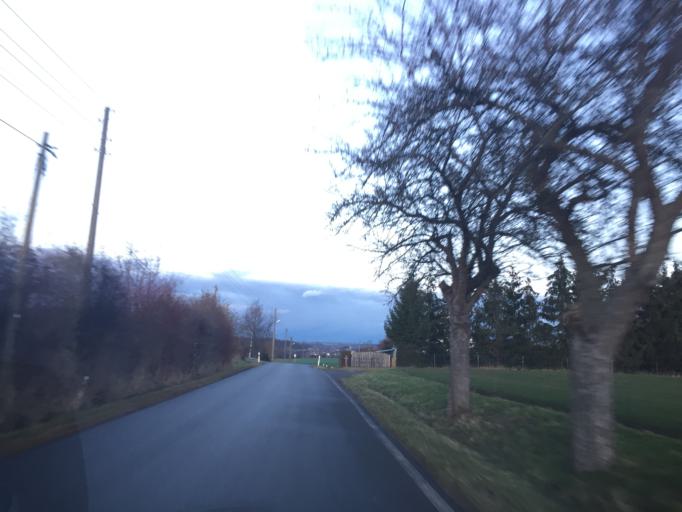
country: DE
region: Thuringia
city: Vollmershain
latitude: 50.8784
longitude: 12.3162
